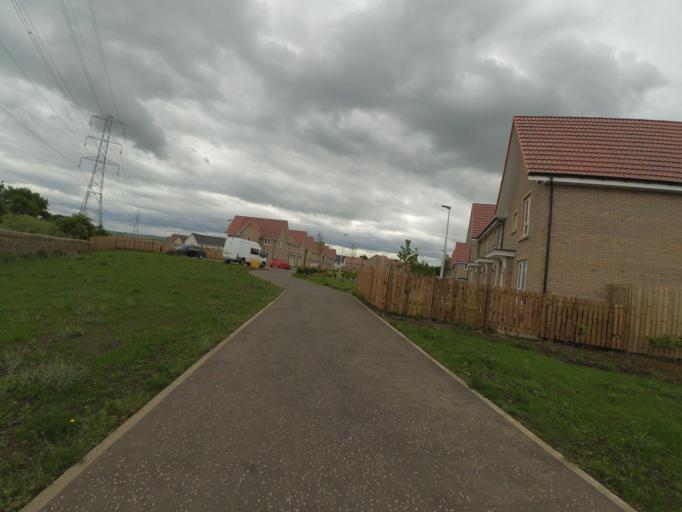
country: GB
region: Scotland
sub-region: East Lothian
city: Musselburgh
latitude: 55.9373
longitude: -3.0915
